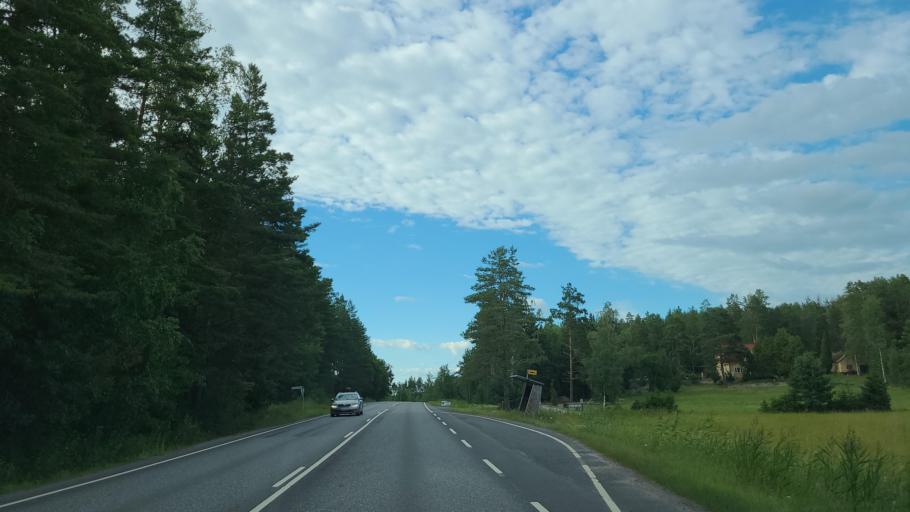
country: FI
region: Varsinais-Suomi
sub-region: Turku
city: Merimasku
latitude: 60.4436
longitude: 21.8974
